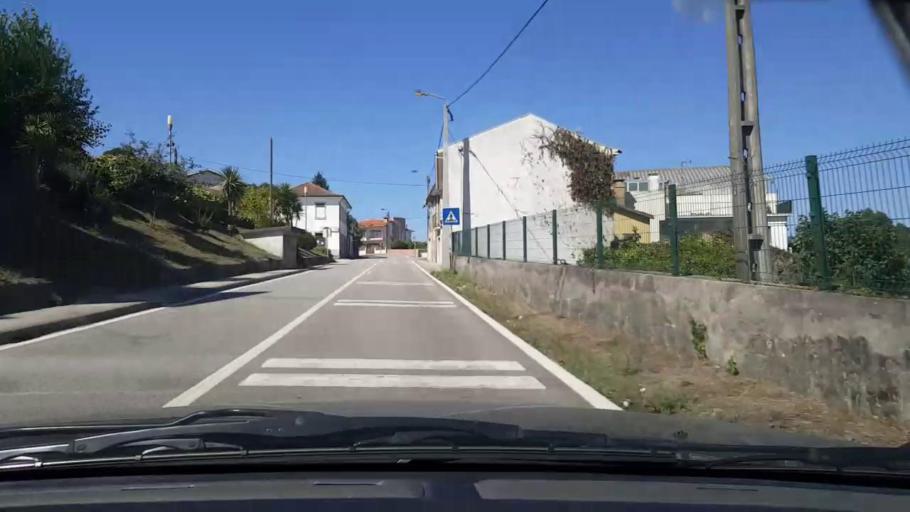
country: PT
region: Porto
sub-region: Maia
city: Gemunde
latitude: 41.3394
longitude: -8.6383
